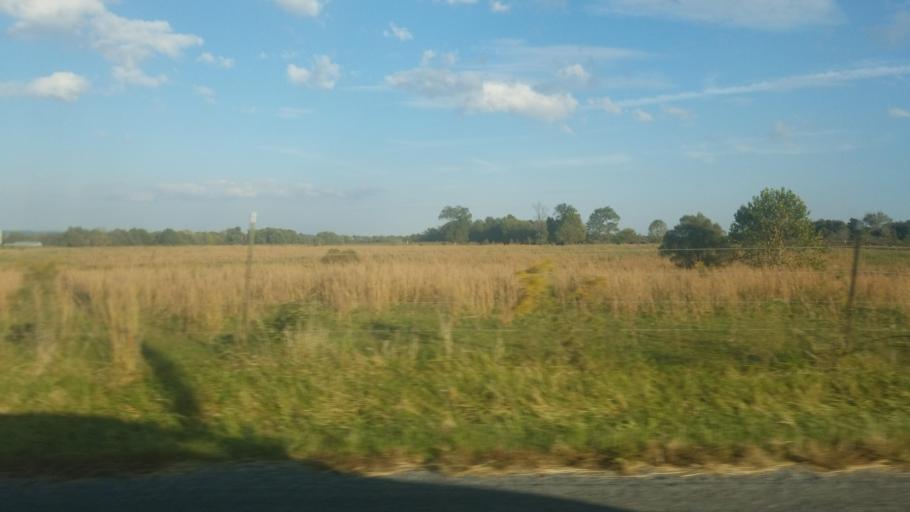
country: US
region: Illinois
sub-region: Saline County
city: Carrier Mills
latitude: 37.7999
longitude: -88.7117
